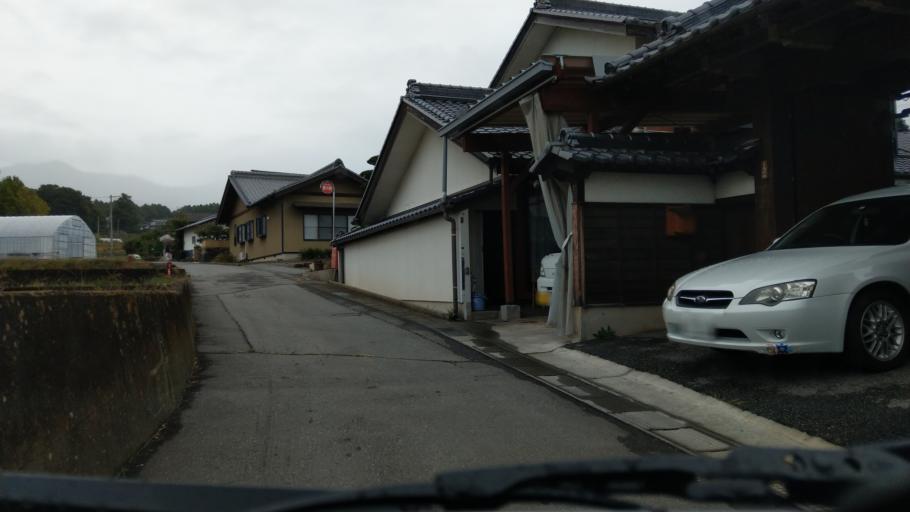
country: JP
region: Nagano
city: Komoro
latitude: 36.3335
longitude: 138.4511
